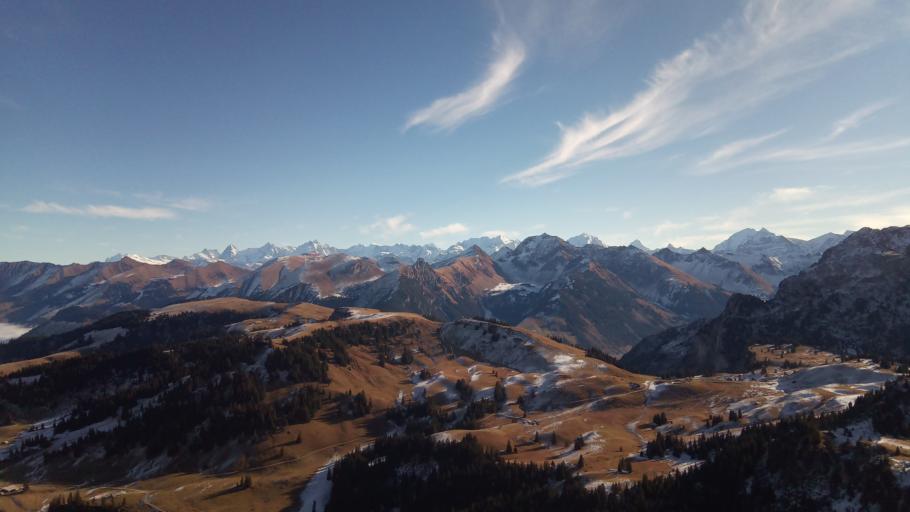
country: CH
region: Bern
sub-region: Obersimmental-Saanen District
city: Boltigen
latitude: 46.5929
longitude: 7.4300
